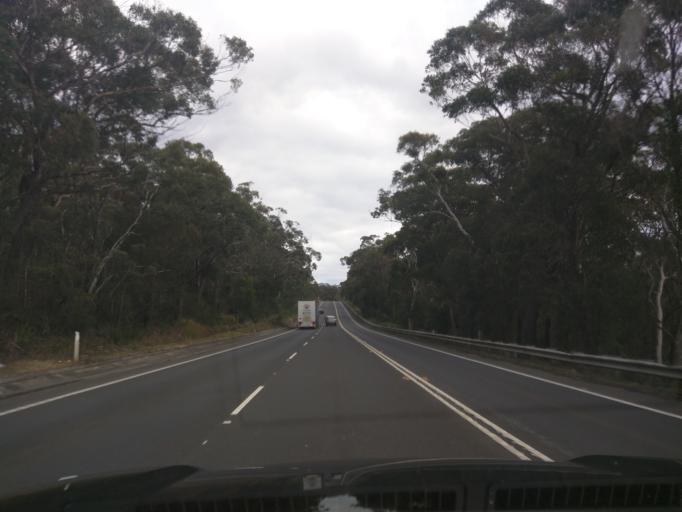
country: AU
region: New South Wales
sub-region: Wollongong
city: Mount Ousley
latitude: -34.3721
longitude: 150.8455
